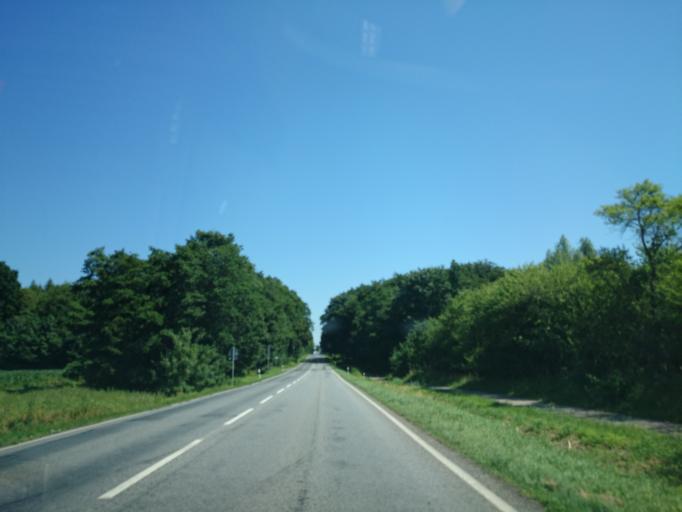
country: DE
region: Mecklenburg-Vorpommern
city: Broderstorf
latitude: 54.0783
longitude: 12.2987
